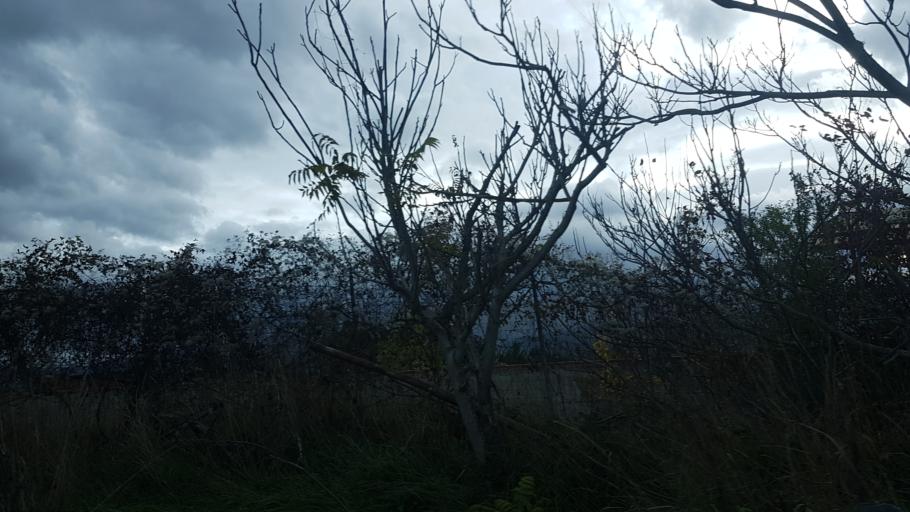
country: IT
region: Abruzzo
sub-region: Provincia dell' Aquila
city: L'Aquila
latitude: 42.3525
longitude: 13.4205
